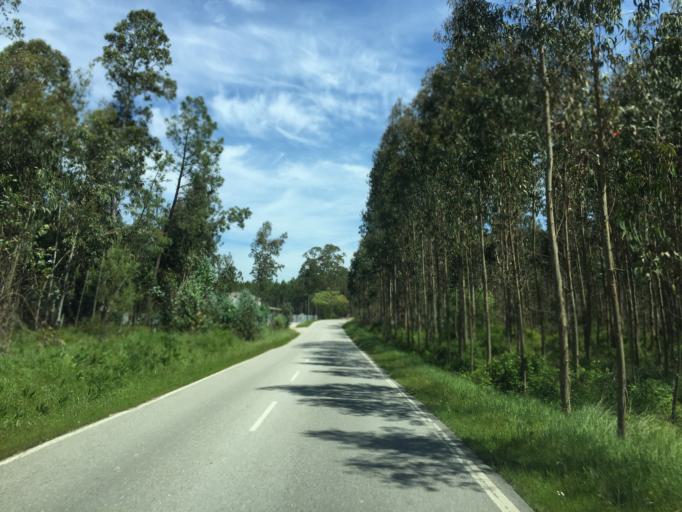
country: PT
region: Coimbra
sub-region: Soure
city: Soure
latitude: 40.0578
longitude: -8.6591
